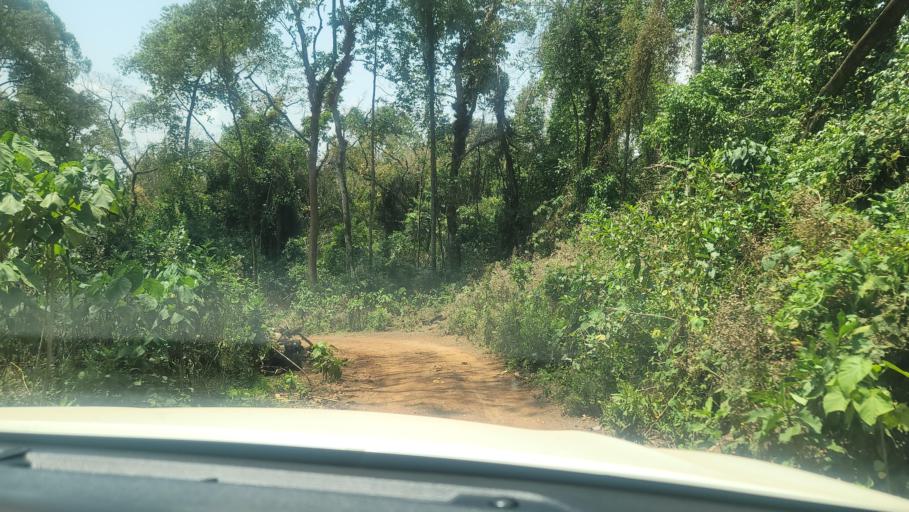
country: ET
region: Southern Nations, Nationalities, and People's Region
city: Bonga
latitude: 7.5474
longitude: 36.1751
